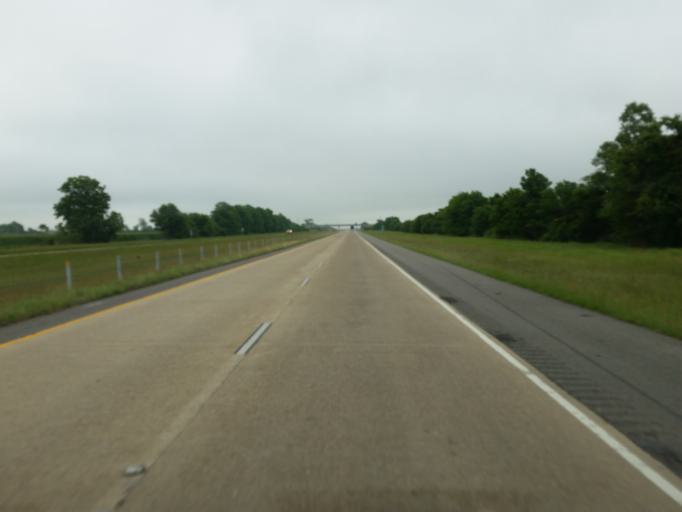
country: US
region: Mississippi
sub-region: Warren County
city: Vicksburg
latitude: 32.3312
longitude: -91.0332
